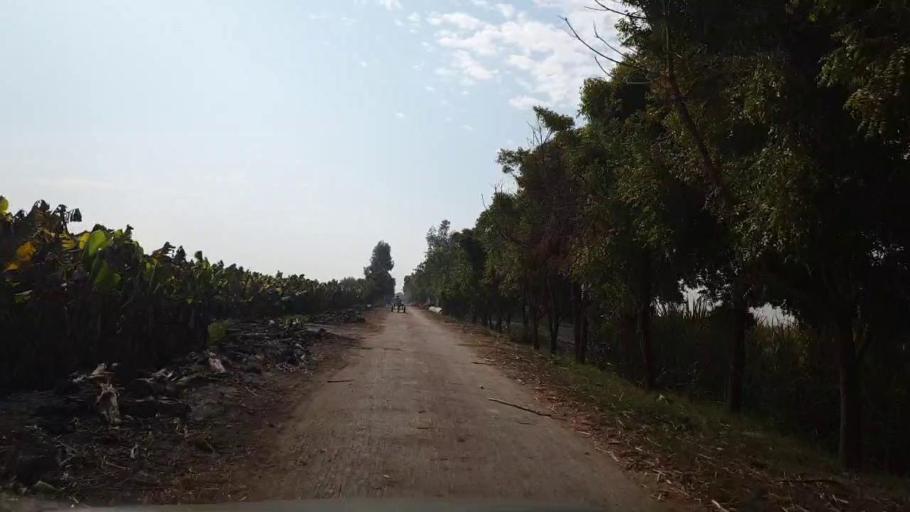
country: PK
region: Sindh
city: Matiari
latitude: 25.5534
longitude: 68.5159
